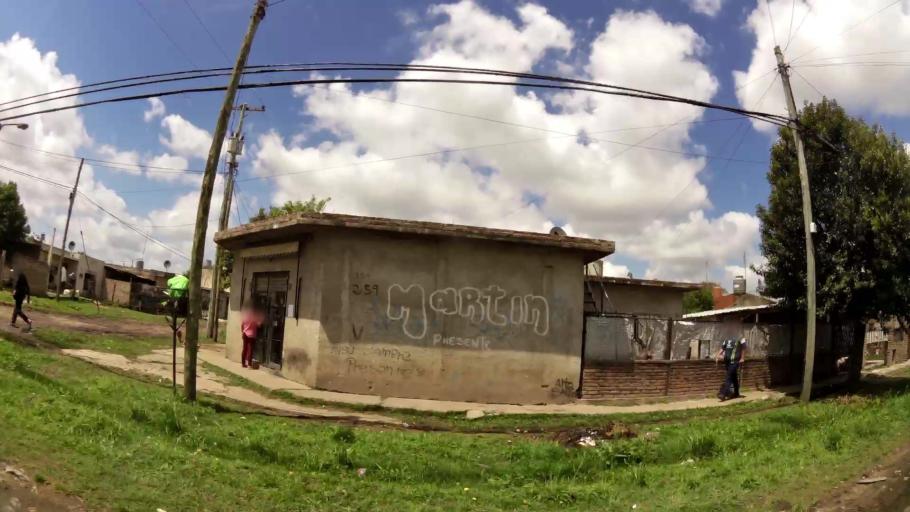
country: AR
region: Buenos Aires
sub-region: Partido de Quilmes
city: Quilmes
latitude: -34.8301
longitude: -58.2422
